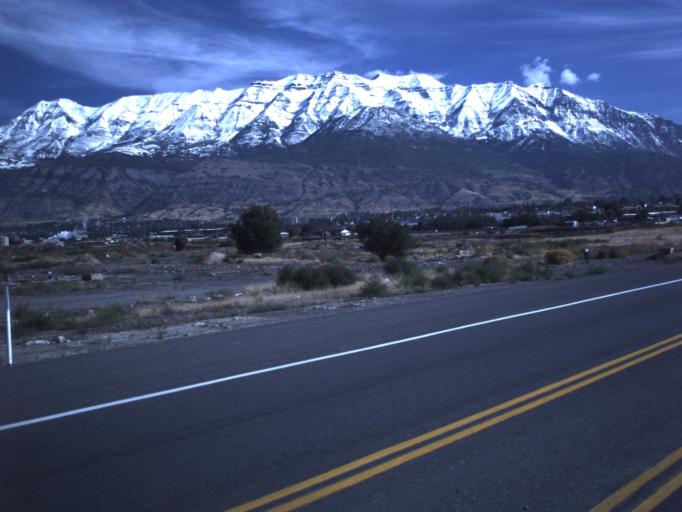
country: US
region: Utah
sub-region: Utah County
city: Lindon
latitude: 40.3117
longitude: -111.7431
